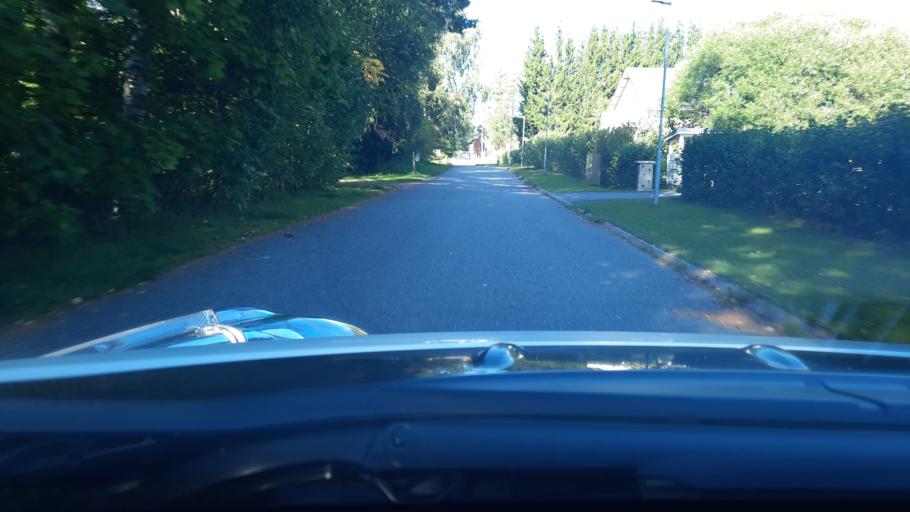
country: FI
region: North Karelia
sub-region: Joensuu
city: Joensuu
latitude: 62.6366
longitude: 29.6850
